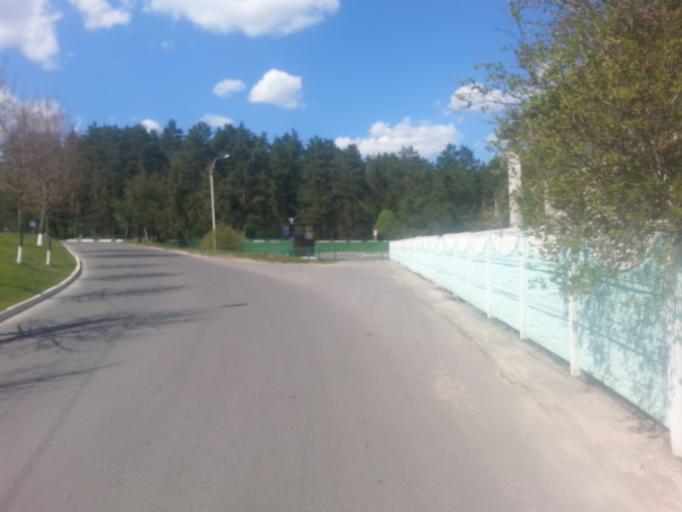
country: BY
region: Minsk
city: Narach
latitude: 54.9134
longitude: 26.7075
